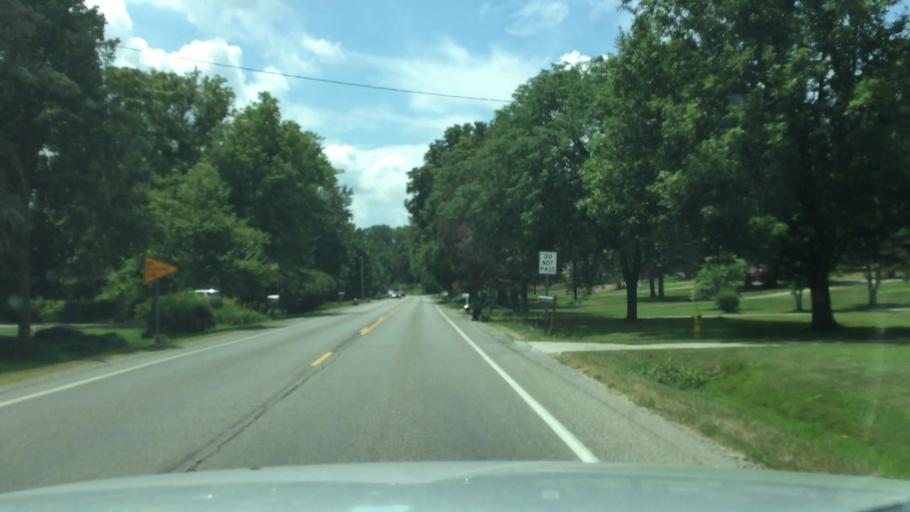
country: US
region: Michigan
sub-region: Genesee County
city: Flushing
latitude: 43.0765
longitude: -83.8716
